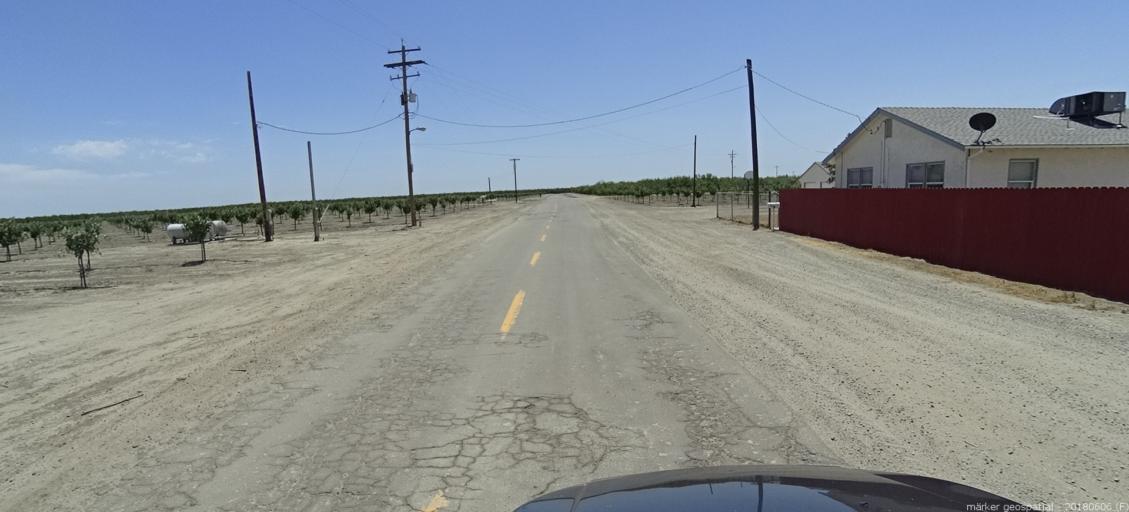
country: US
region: California
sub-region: Fresno County
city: Firebaugh
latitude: 36.8342
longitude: -120.3809
